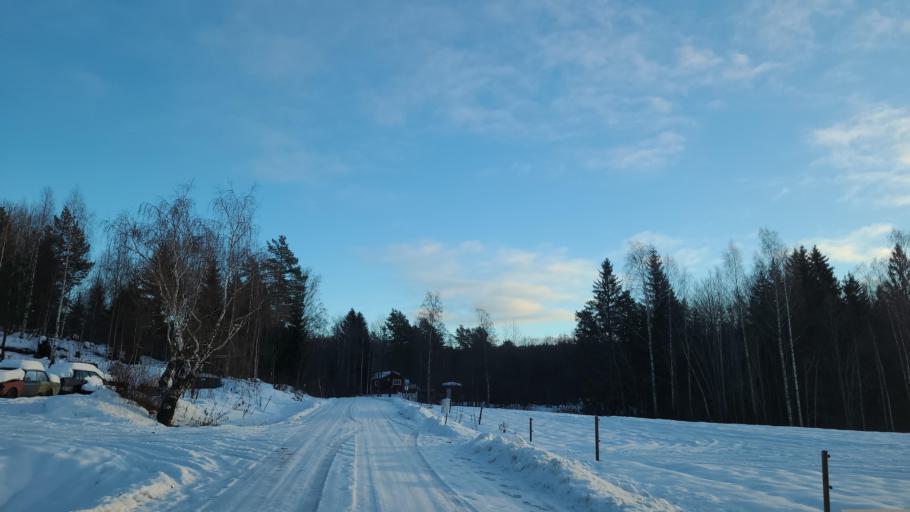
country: SE
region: Gaevleborg
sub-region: Bollnas Kommun
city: Kilafors
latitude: 61.3944
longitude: 16.6873
